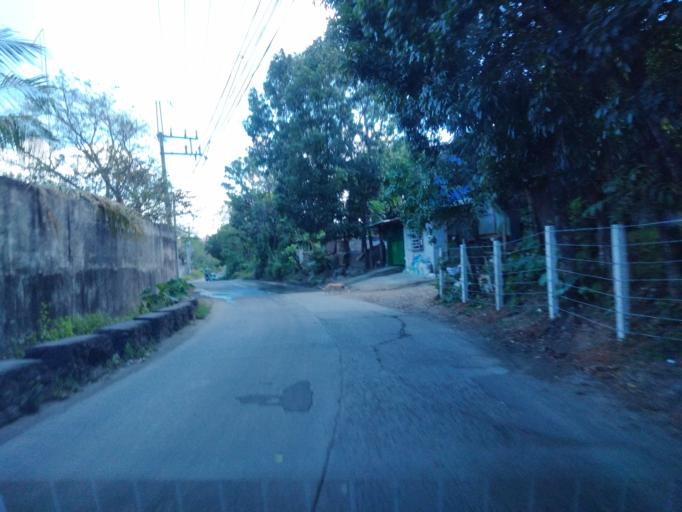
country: PH
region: Central Luzon
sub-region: Province of Bulacan
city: Bitungol
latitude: 14.8582
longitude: 121.0422
